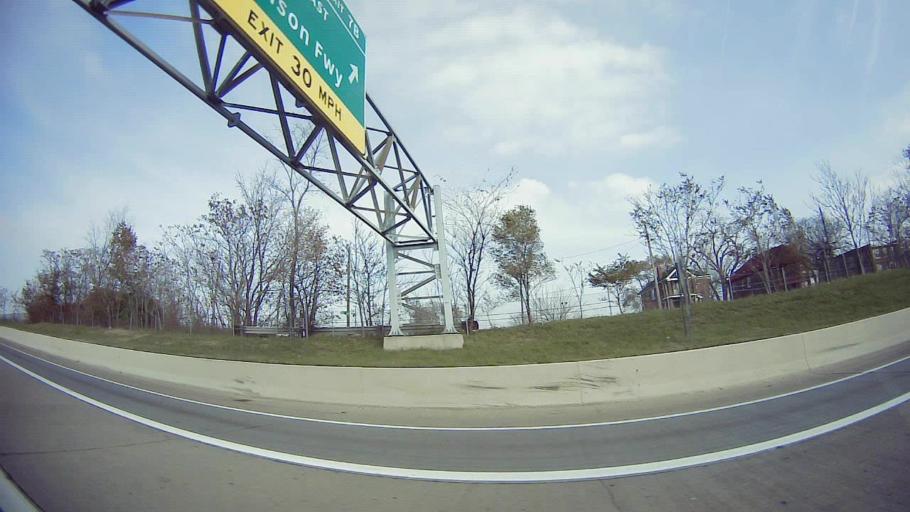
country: US
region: Michigan
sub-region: Wayne County
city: Highland Park
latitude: 42.3964
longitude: -83.1082
